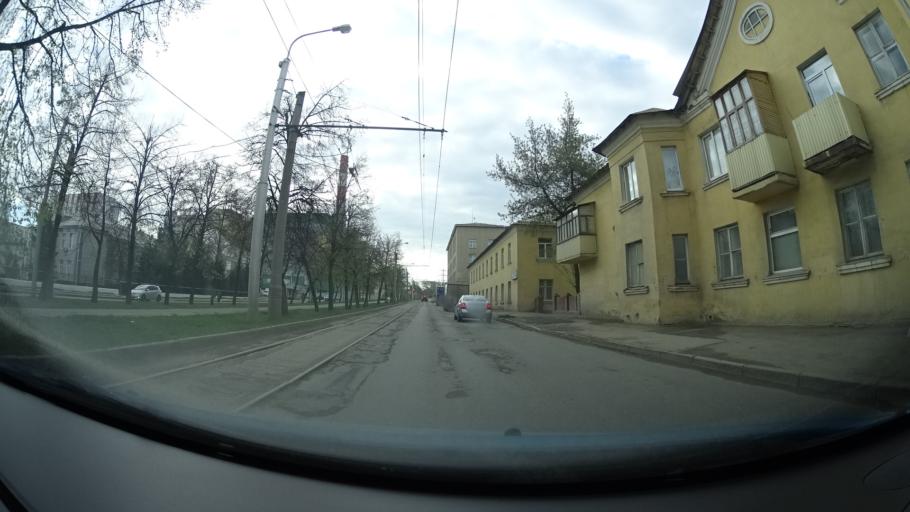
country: RU
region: Bashkortostan
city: Ufa
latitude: 54.7410
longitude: 55.9643
